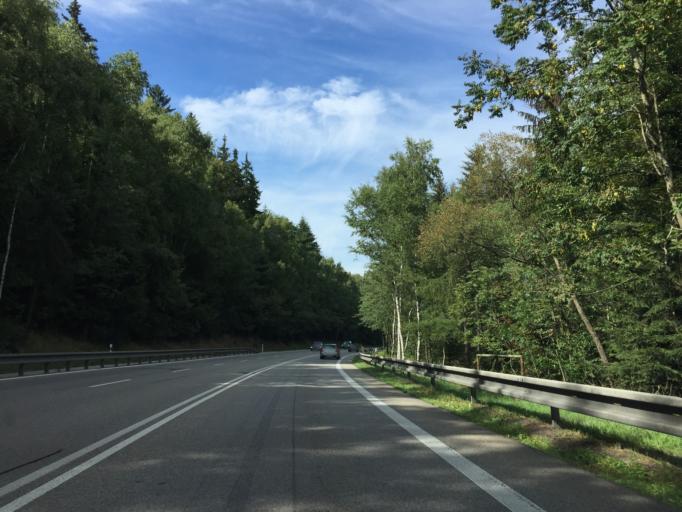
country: CZ
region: Central Bohemia
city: Votice
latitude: 49.6254
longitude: 14.6513
